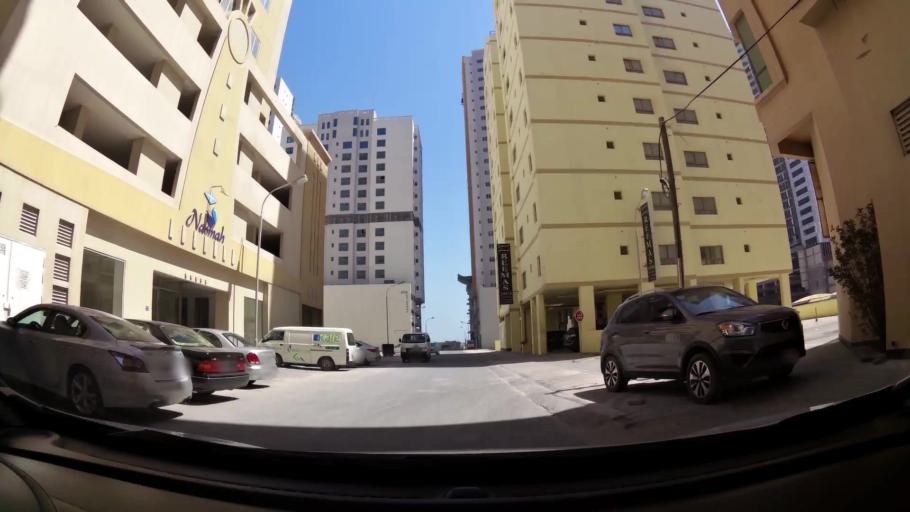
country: BH
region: Manama
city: Manama
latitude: 26.2221
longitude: 50.6095
